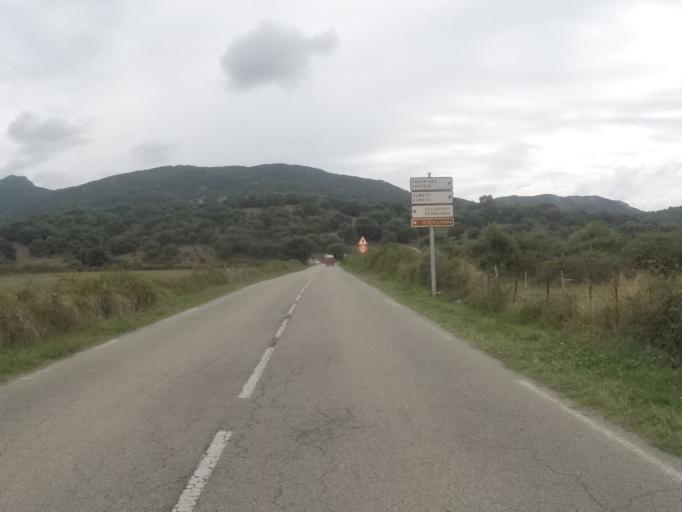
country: FR
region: Corsica
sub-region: Departement de la Corse-du-Sud
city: Propriano
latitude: 41.7225
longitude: 8.8363
